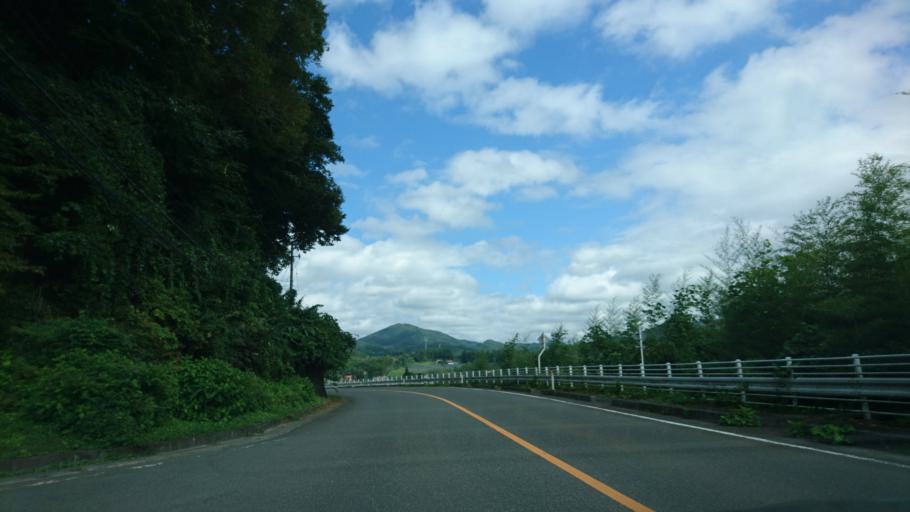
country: JP
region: Miyagi
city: Furukawa
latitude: 38.7859
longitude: 140.8466
